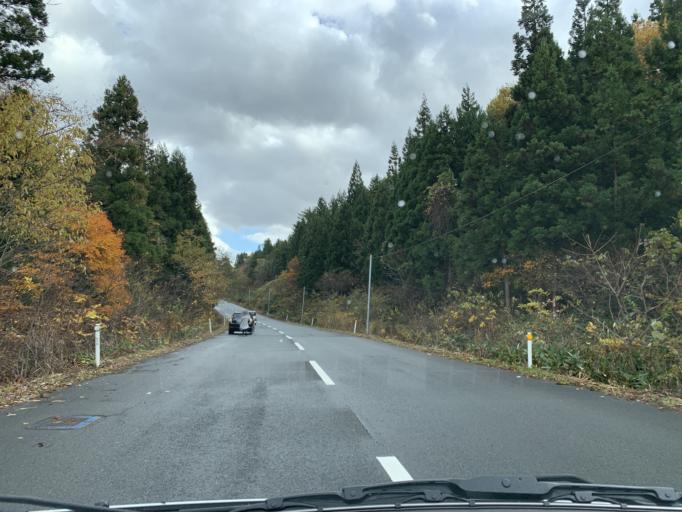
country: JP
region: Iwate
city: Mizusawa
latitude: 39.1144
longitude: 140.9467
